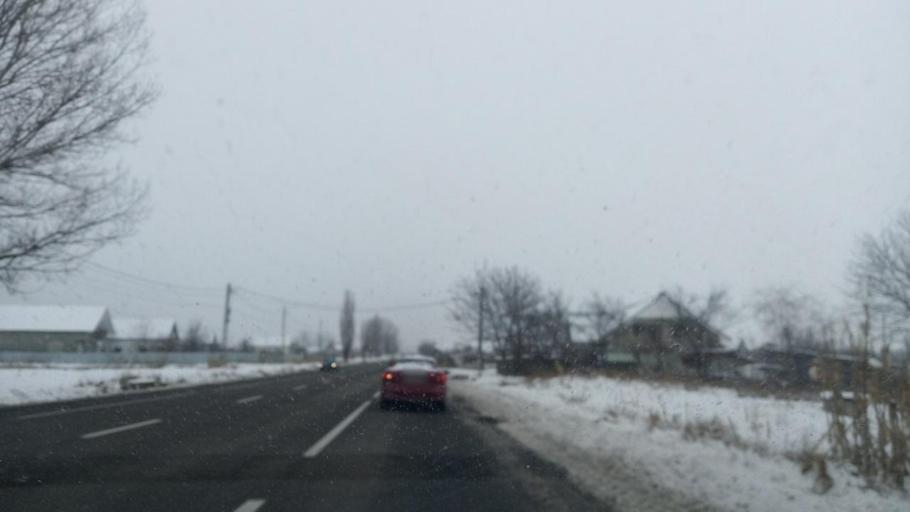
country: RO
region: Bacau
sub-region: Comuna Racaciuni
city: Gheorghe Doja
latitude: 46.3948
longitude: 26.9492
